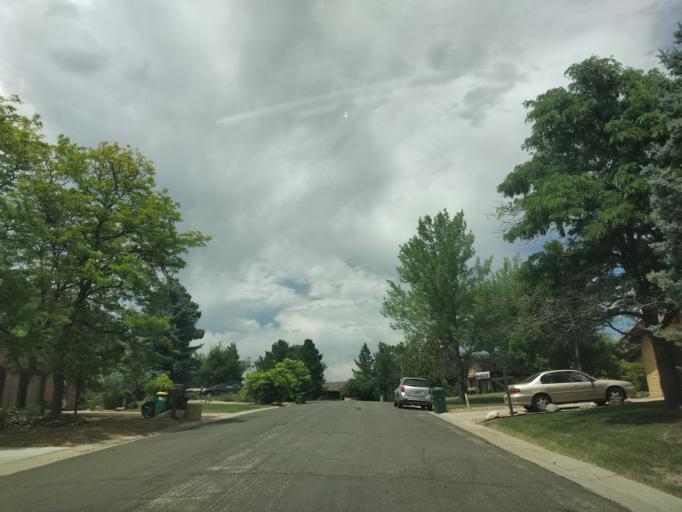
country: US
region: Colorado
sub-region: Jefferson County
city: Lakewood
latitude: 39.6868
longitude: -105.1269
